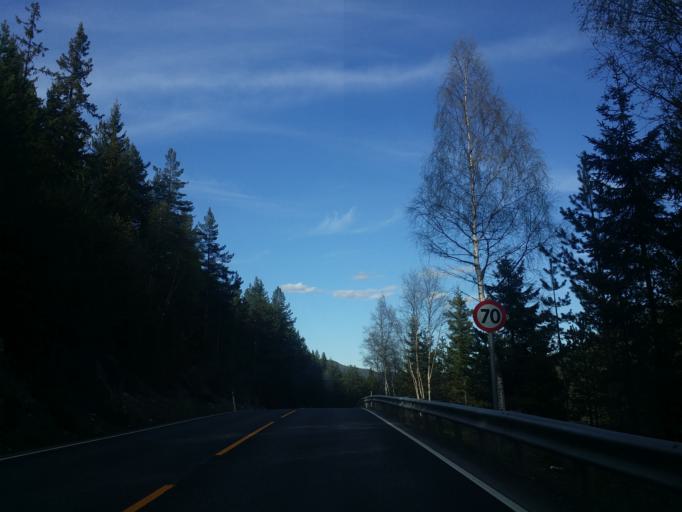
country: NO
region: Buskerud
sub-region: Kongsberg
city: Kongsberg
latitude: 59.6173
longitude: 9.4686
